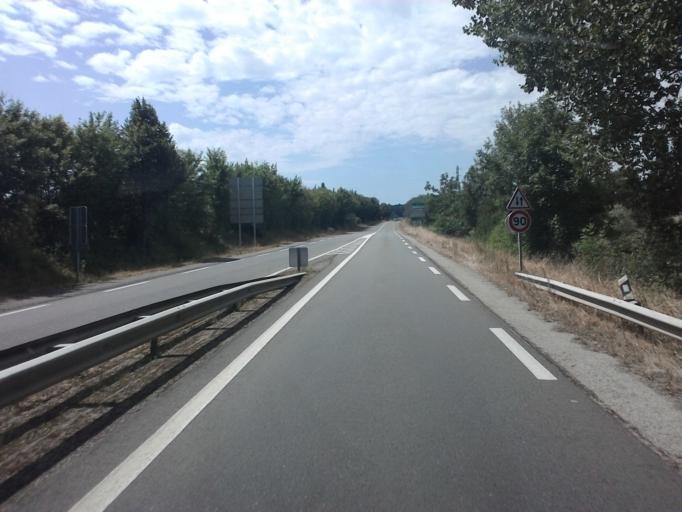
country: FR
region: Bourgogne
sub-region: Departement de Saone-et-Loire
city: Cuiseaux
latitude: 46.4868
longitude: 5.3727
